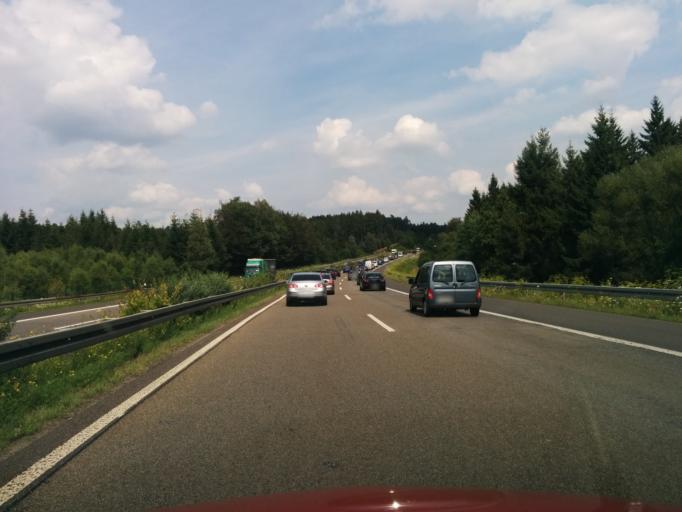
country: DE
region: Hesse
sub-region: Regierungsbezirk Kassel
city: Ottrau
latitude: 50.7775
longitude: 9.3975
